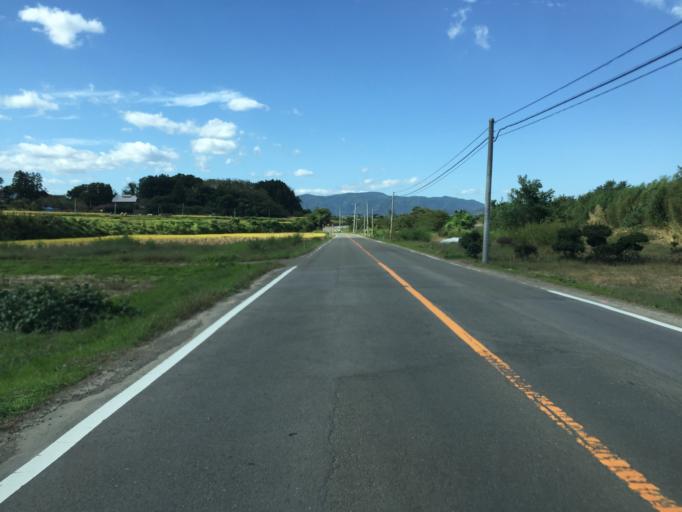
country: JP
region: Fukushima
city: Yanagawamachi-saiwaicho
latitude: 37.8367
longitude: 140.6164
